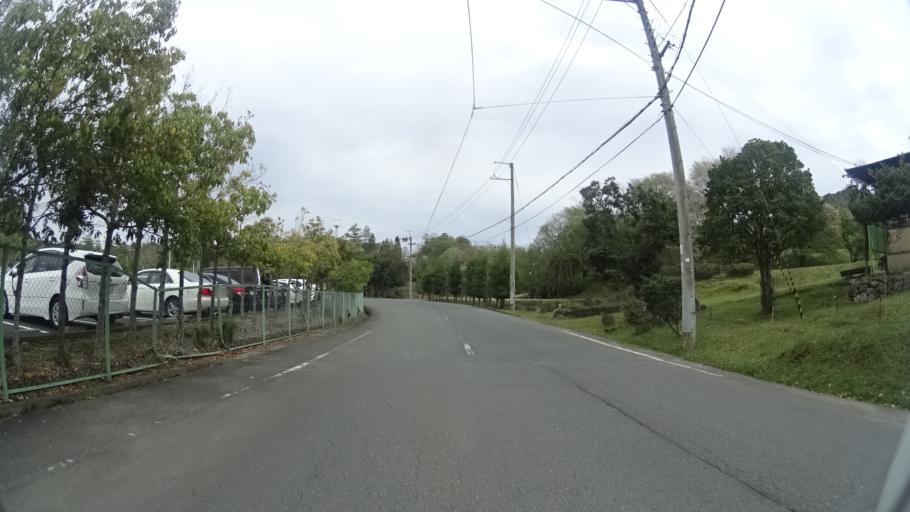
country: JP
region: Kyoto
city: Kameoka
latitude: 35.1638
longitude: 135.4487
